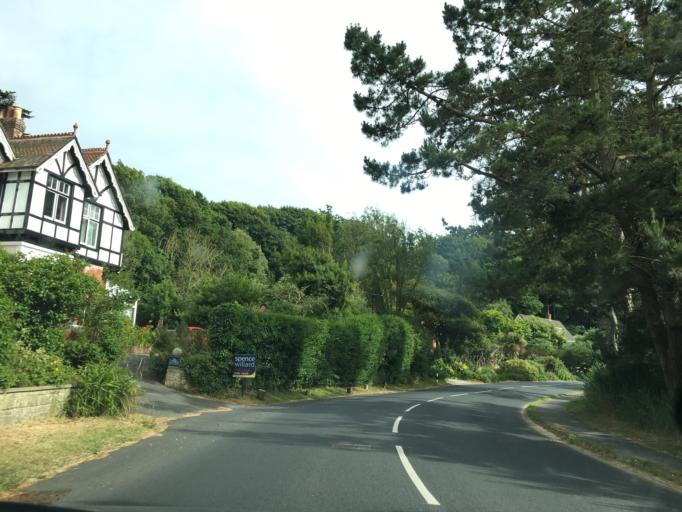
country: GB
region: England
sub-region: Isle of Wight
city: Freshwater
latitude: 50.6737
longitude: -1.5068
